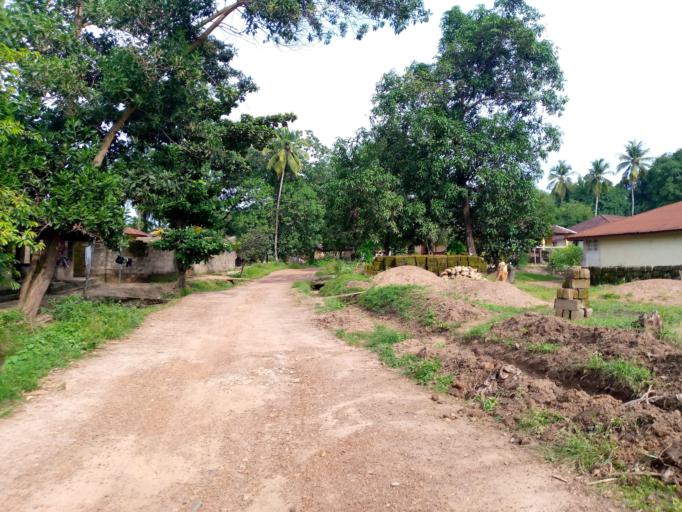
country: SL
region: Northern Province
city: Magburaka
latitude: 8.7194
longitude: -11.9512
